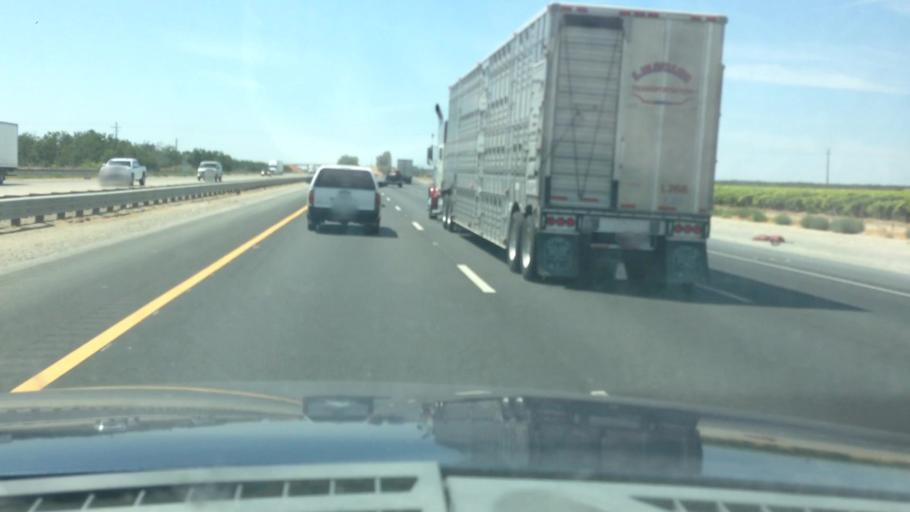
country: US
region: California
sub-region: Kern County
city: McFarland
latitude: 35.6550
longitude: -119.2220
